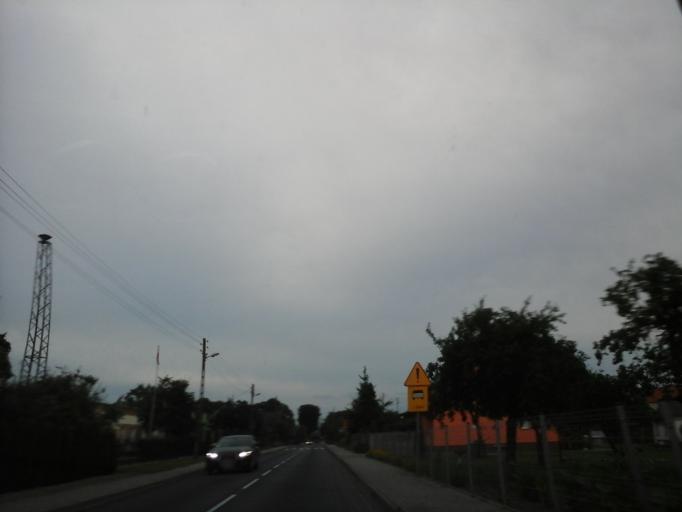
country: PL
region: West Pomeranian Voivodeship
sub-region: Powiat goleniowski
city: Maszewo
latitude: 53.4539
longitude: 15.0619
